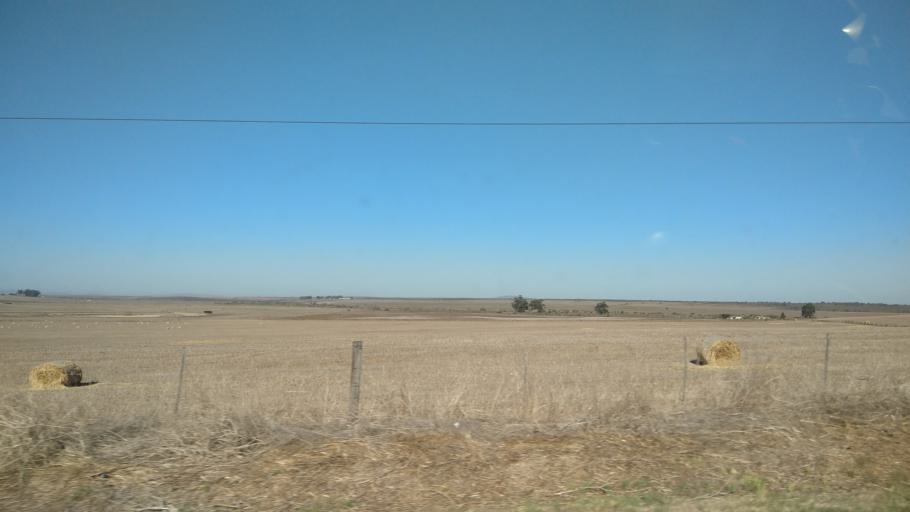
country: ZA
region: Western Cape
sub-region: West Coast District Municipality
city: Moorreesburg
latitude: -33.1224
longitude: 18.4425
